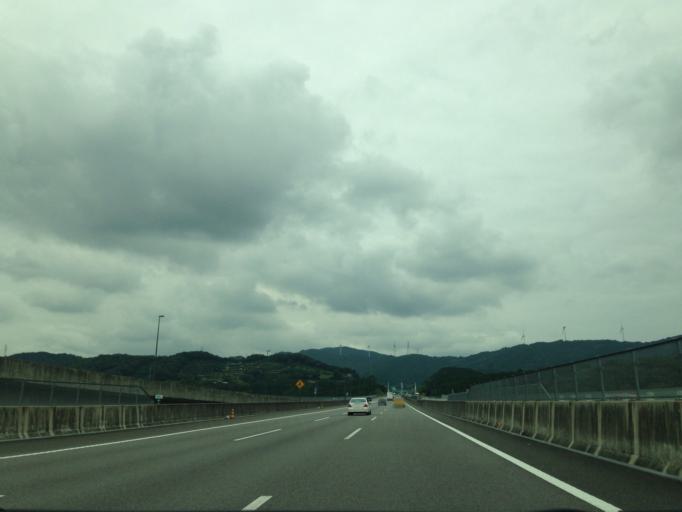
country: JP
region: Shizuoka
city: Hamakita
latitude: 34.8441
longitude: 137.7416
